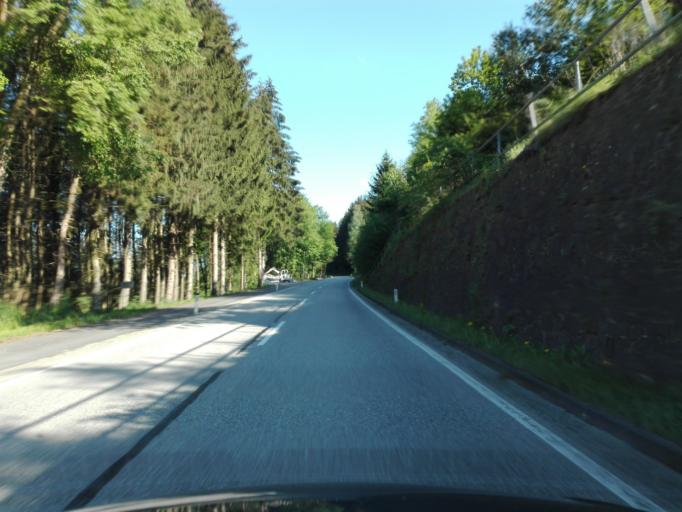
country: AT
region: Upper Austria
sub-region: Politischer Bezirk Rohrbach
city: Pfarrkirchen im Muehlkreis
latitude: 48.4887
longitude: 13.7456
